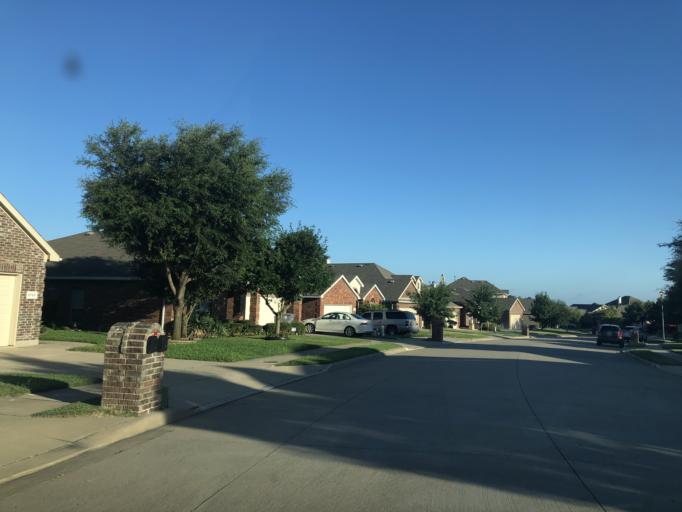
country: US
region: Texas
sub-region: Dallas County
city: Duncanville
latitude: 32.6505
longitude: -96.9497
